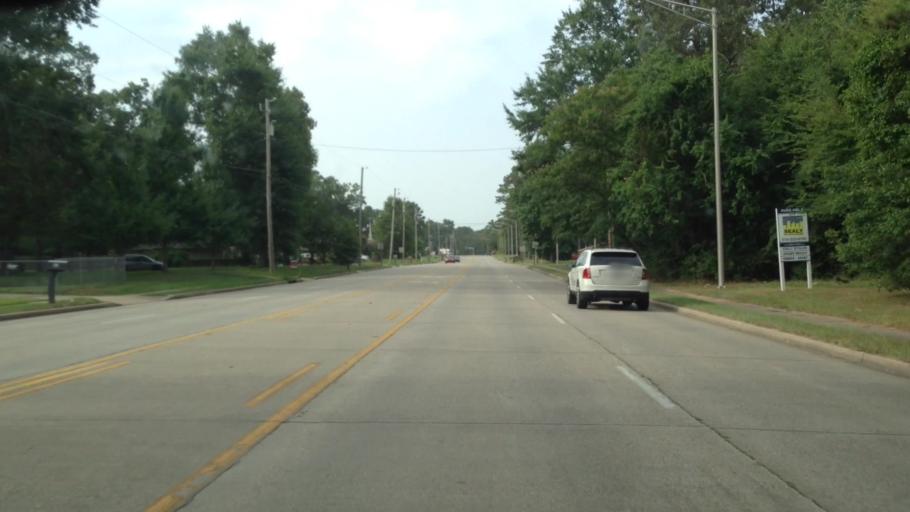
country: US
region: Louisiana
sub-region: De Soto Parish
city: Stonewall
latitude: 32.3998
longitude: -93.8147
